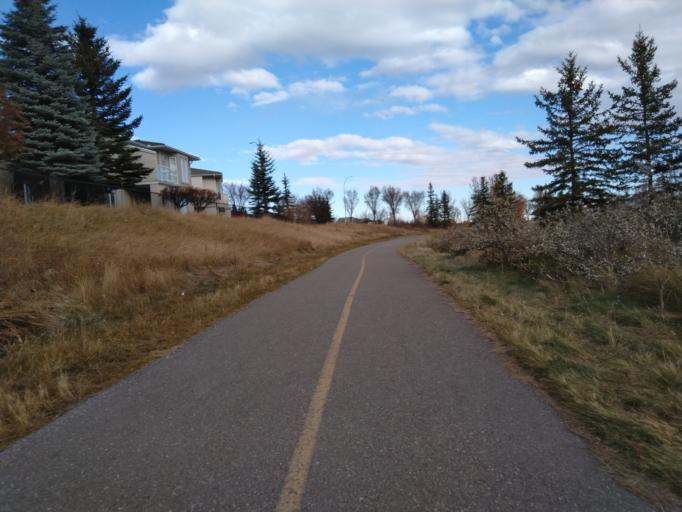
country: CA
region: Alberta
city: Calgary
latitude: 51.1386
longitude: -114.1318
